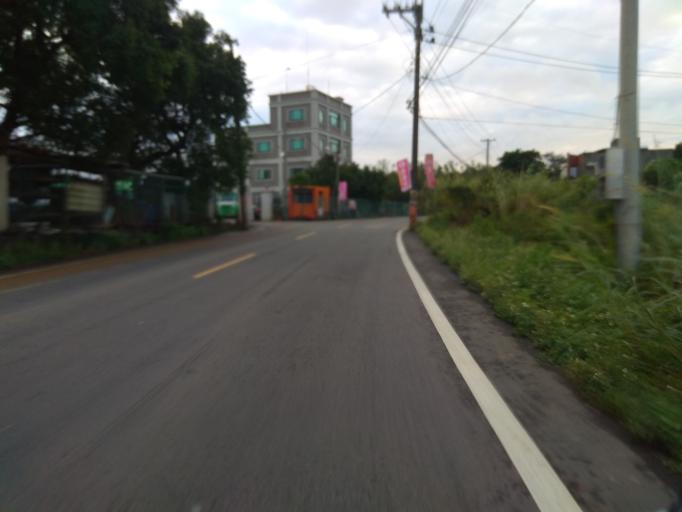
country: TW
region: Taiwan
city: Taoyuan City
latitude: 24.9480
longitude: 121.1906
